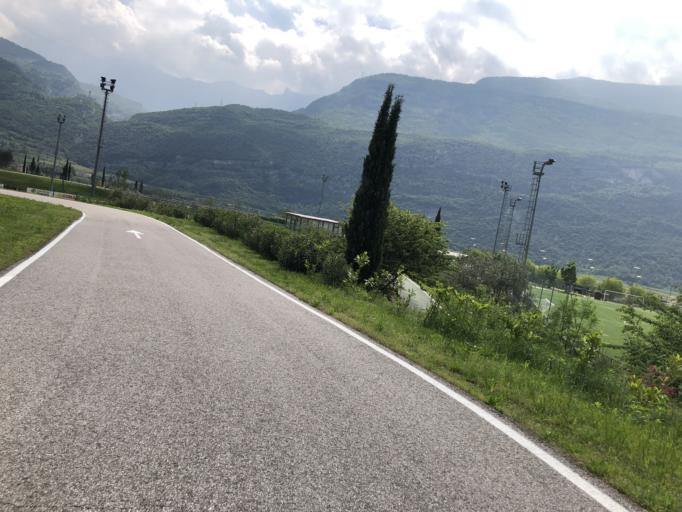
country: IT
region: Trentino-Alto Adige
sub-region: Provincia di Trento
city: Dro
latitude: 45.9692
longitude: 10.9128
